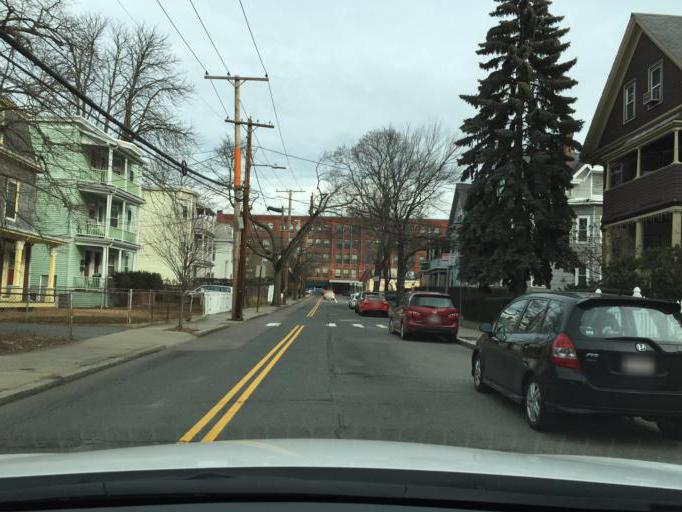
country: US
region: Massachusetts
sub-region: Middlesex County
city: Cambridge
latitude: 42.3903
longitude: -71.1241
